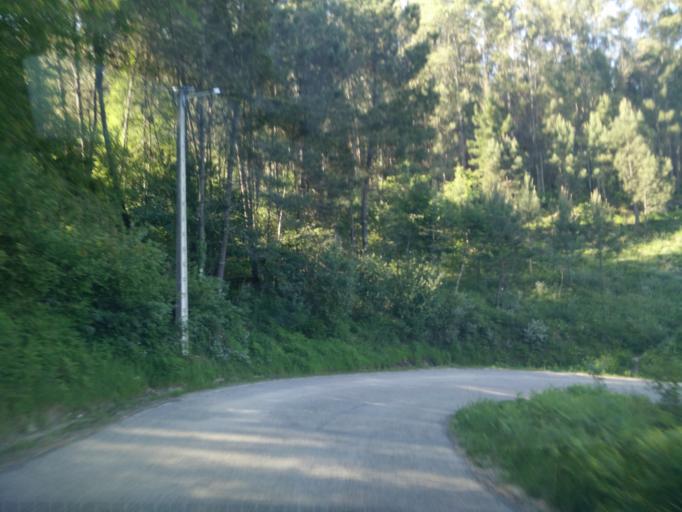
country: ES
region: Galicia
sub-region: Provincia de Pontevedra
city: Mondariz
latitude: 42.2603
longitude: -8.4136
